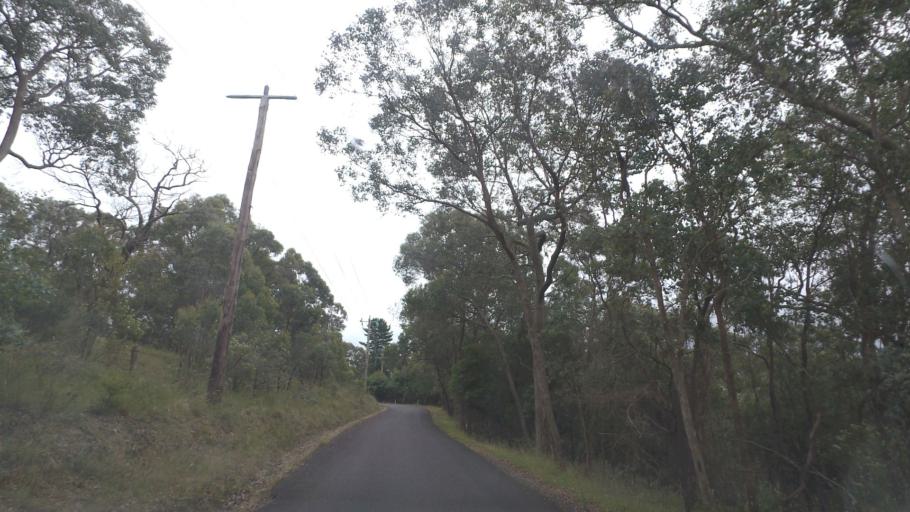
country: AU
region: Victoria
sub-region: Manningham
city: Warrandyte
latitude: -37.7599
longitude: 145.2213
